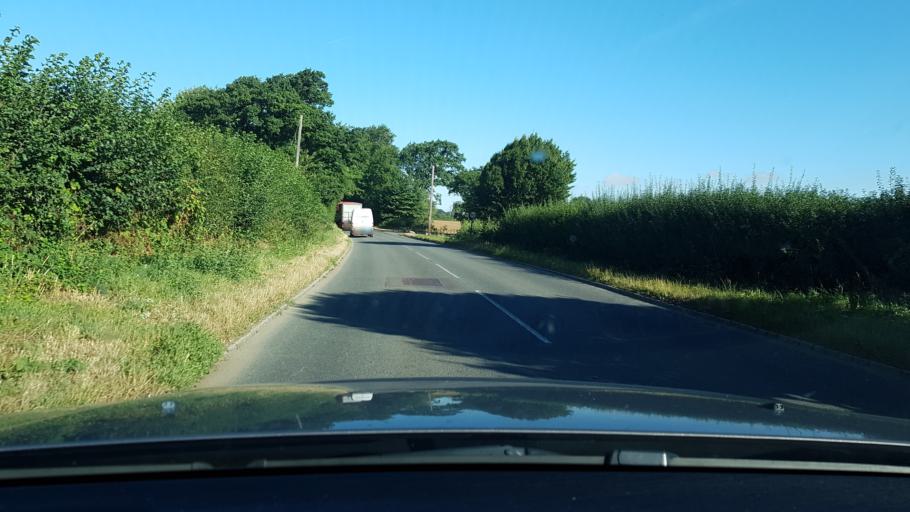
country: GB
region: England
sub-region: West Berkshire
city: Wickham
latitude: 51.4601
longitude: -1.4830
